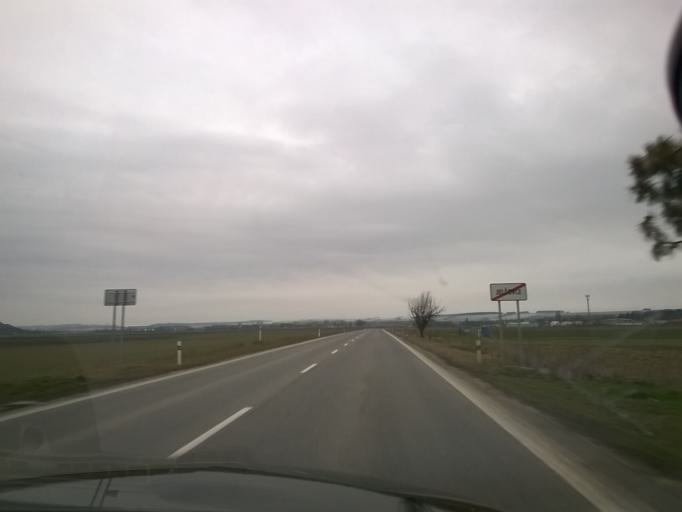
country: SK
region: Nitriansky
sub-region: Okres Nitra
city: Nitra
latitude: 48.3789
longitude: 18.0526
